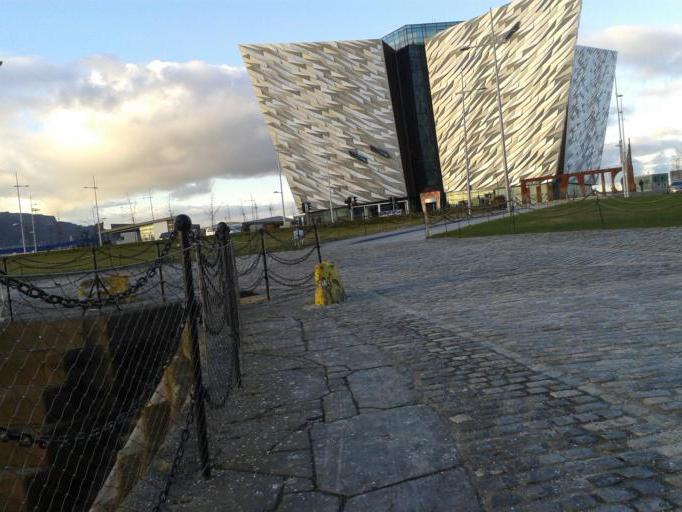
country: GB
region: Northern Ireland
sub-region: City of Belfast
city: Belfast
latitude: 54.6066
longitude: -5.9105
